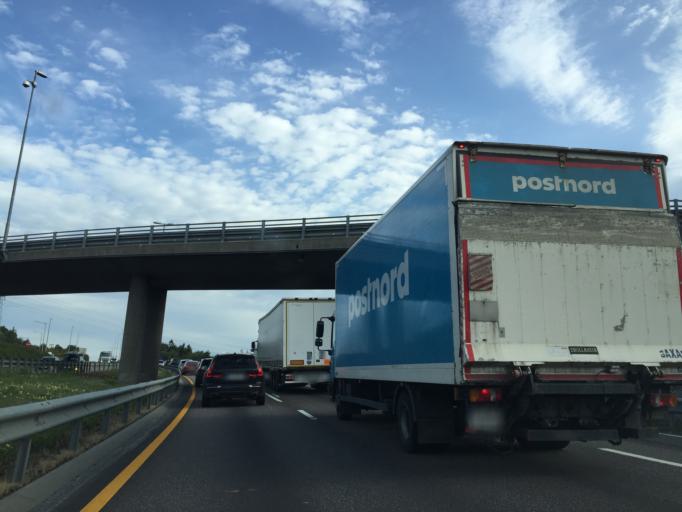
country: NO
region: Akershus
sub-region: Oppegard
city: Kolbotn
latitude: 59.8388
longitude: 10.8399
